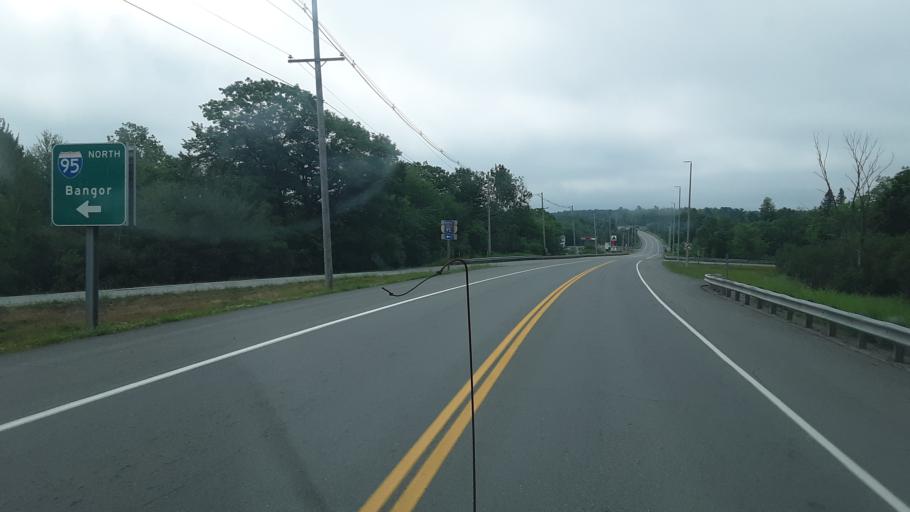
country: US
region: Maine
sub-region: Penobscot County
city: Hampden
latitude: 44.7728
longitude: -68.8586
